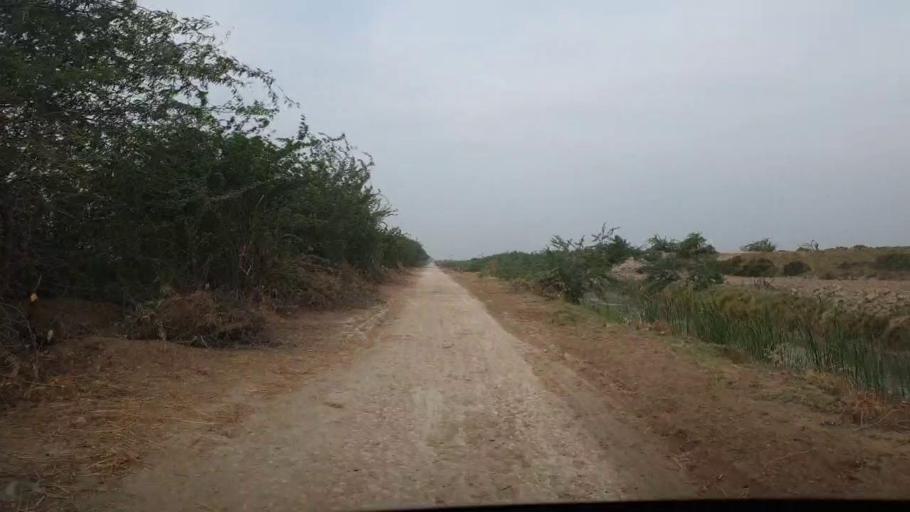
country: PK
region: Sindh
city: Chuhar Jamali
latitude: 24.4071
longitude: 67.9538
